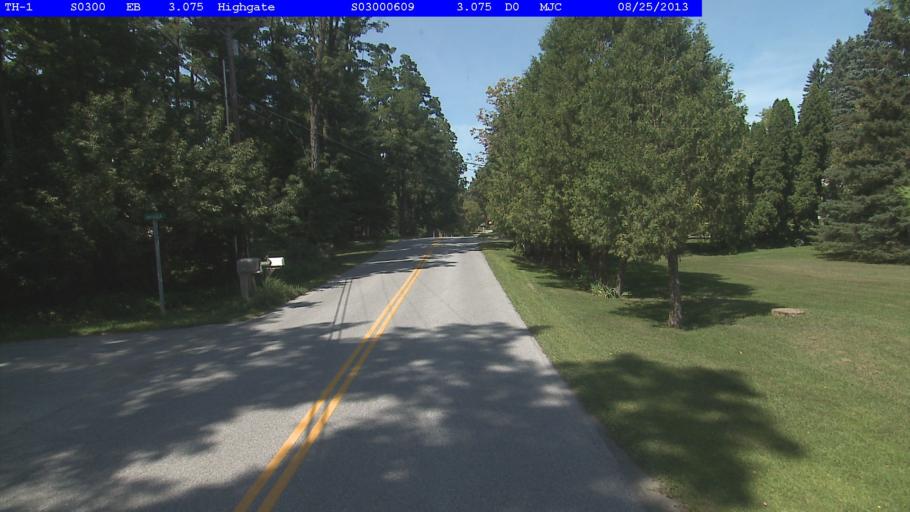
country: US
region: Vermont
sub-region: Franklin County
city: Swanton
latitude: 44.9655
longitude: -73.1007
